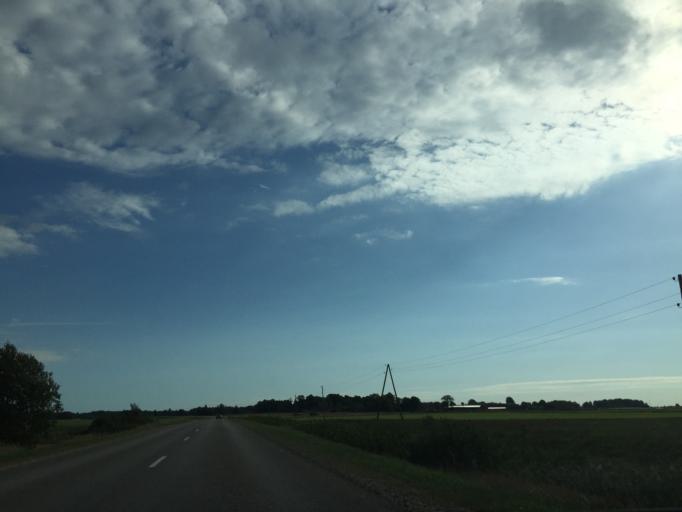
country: LV
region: Limbazu Rajons
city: Limbazi
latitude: 57.5035
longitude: 24.4853
